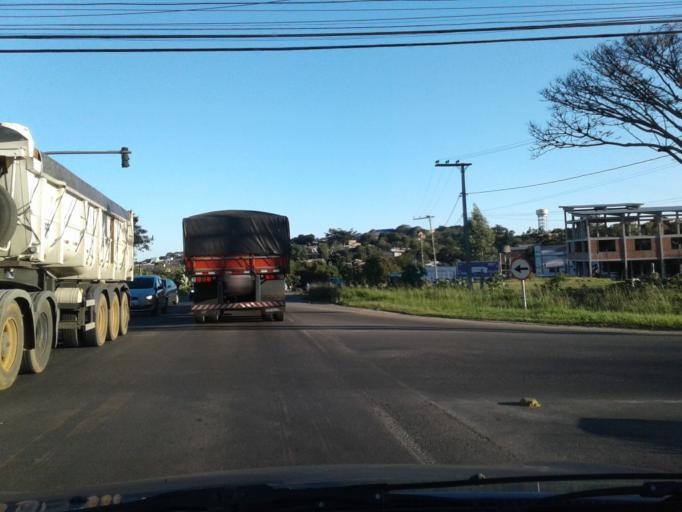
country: BR
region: Rio Grande do Sul
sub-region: Viamao
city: Viamao
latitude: -30.0809
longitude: -51.0173
